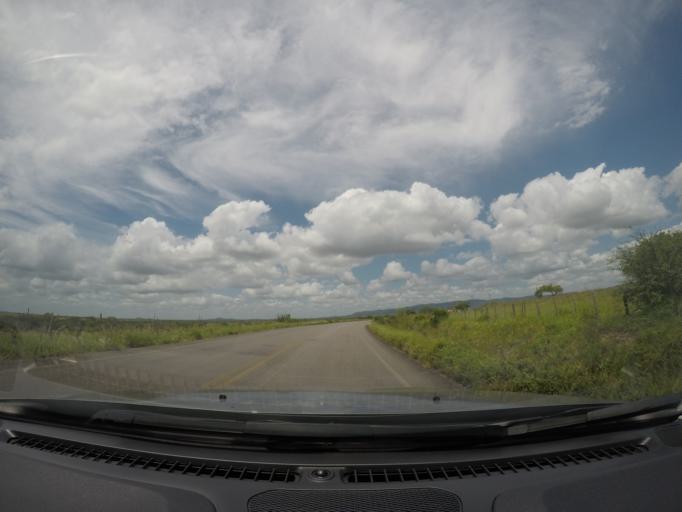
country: BR
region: Bahia
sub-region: Ipira
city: Ipira
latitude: -12.2203
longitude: -39.7877
